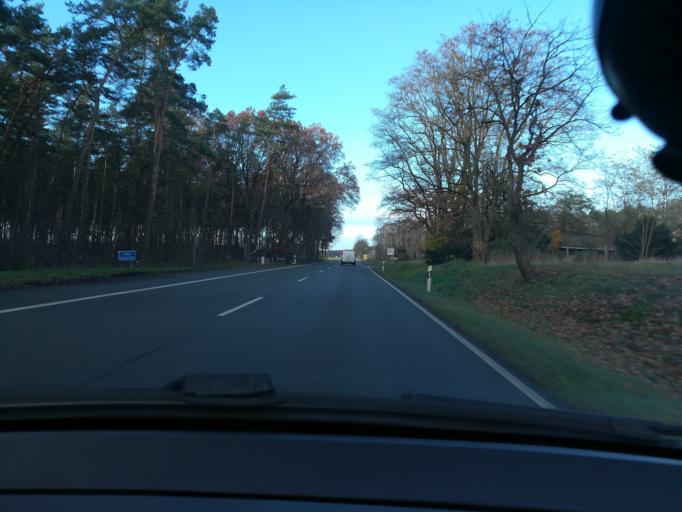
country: DE
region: Lower Saxony
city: Kirchdorf
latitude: 52.5482
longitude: 8.8627
